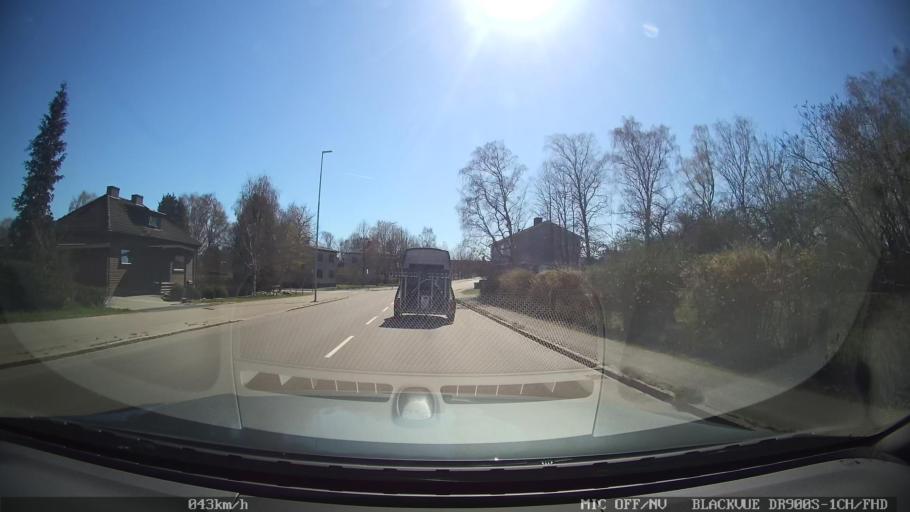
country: SE
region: Skane
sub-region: Klippans Kommun
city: Ljungbyhed
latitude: 56.0781
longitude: 13.2362
